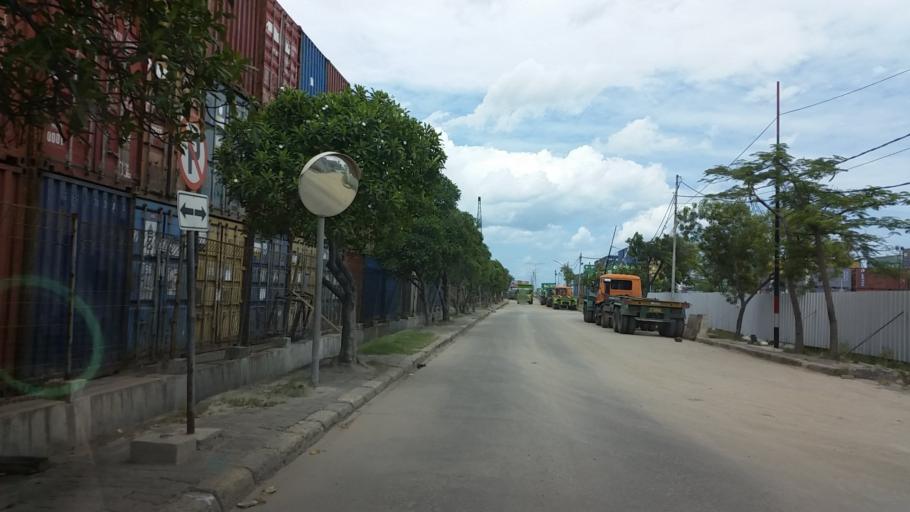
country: ID
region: Jakarta Raya
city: Jakarta
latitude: -6.1230
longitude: 106.8095
